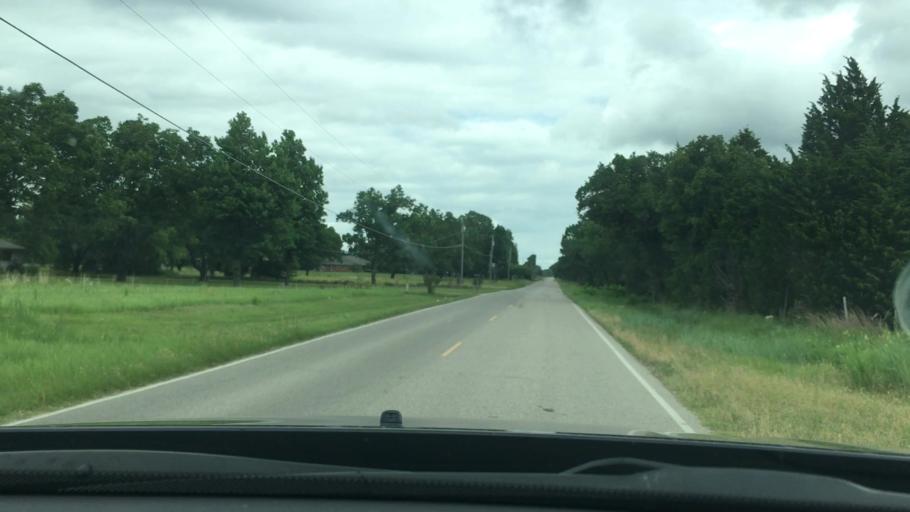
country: US
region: Oklahoma
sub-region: Carter County
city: Ardmore
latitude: 34.1325
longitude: -97.0730
